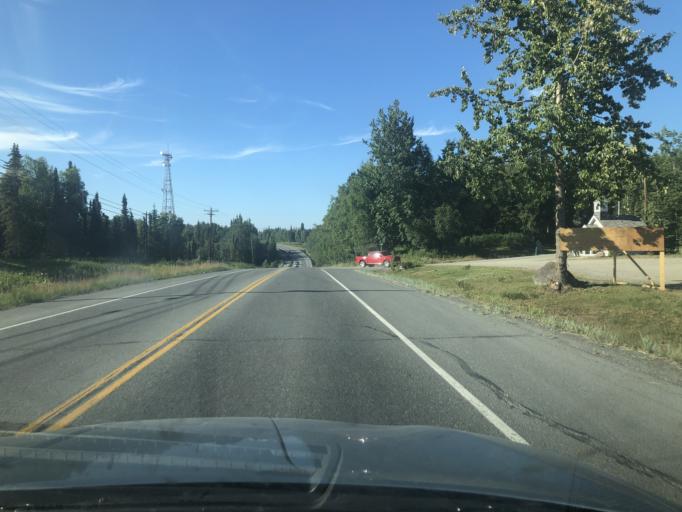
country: US
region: Alaska
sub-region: Kenai Peninsula Borough
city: Ridgeway
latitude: 60.5268
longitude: -151.0809
